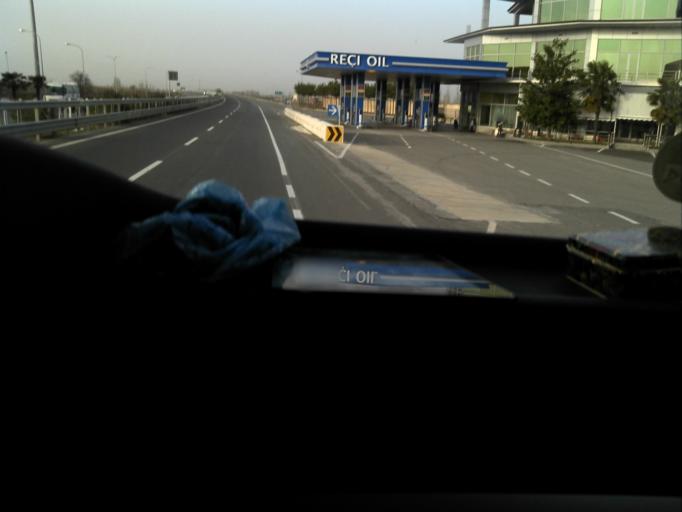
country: AL
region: Lezhe
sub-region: Rrethi i Kurbinit
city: Mamurras
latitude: 41.5738
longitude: 19.6749
